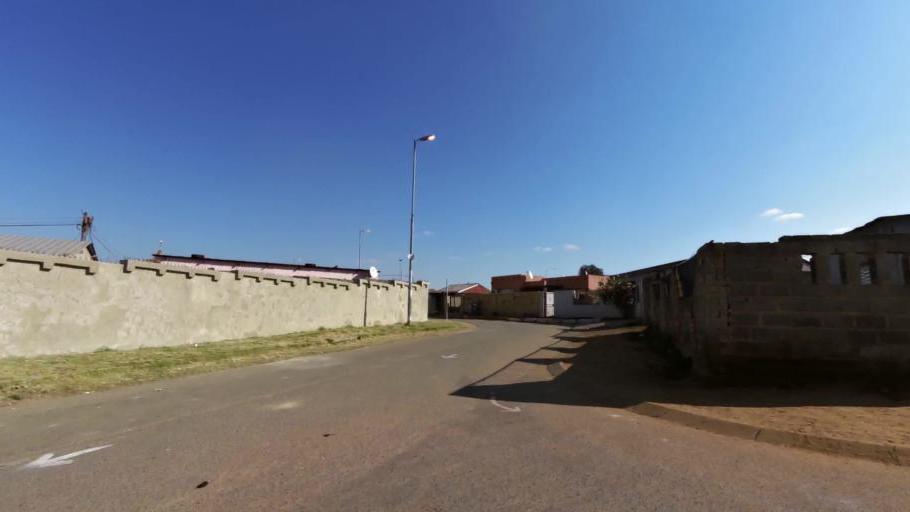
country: ZA
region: Gauteng
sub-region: City of Johannesburg Metropolitan Municipality
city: Soweto
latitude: -26.2493
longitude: 27.9318
